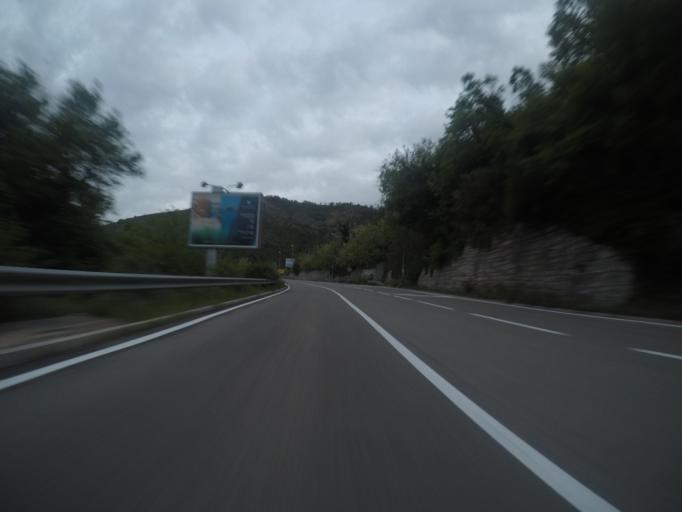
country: ME
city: Petrovac na Moru
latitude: 42.2100
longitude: 18.9458
